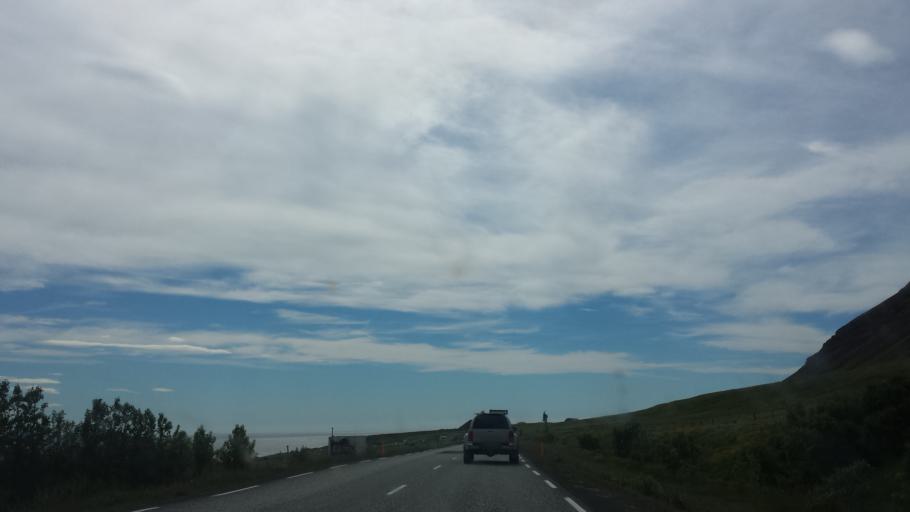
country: IS
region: Capital Region
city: Reykjavik
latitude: 64.3234
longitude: -21.8745
